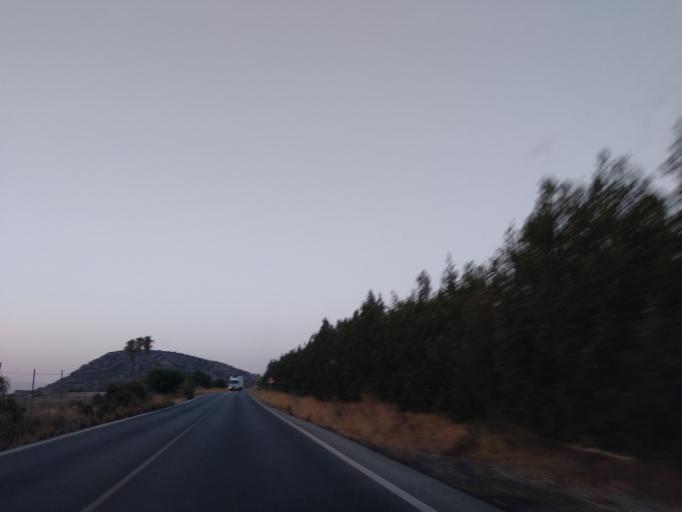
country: ES
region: Andalusia
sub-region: Provincia de Malaga
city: Cartama
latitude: 36.6837
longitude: -4.6556
